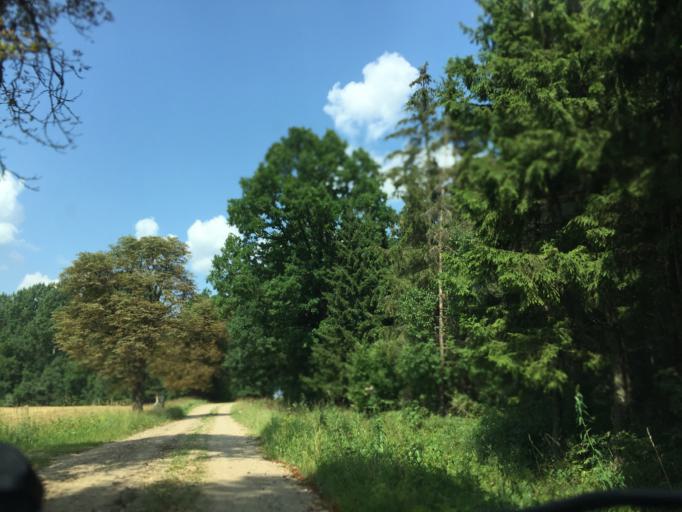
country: LT
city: Zagare
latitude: 56.3894
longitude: 23.2052
